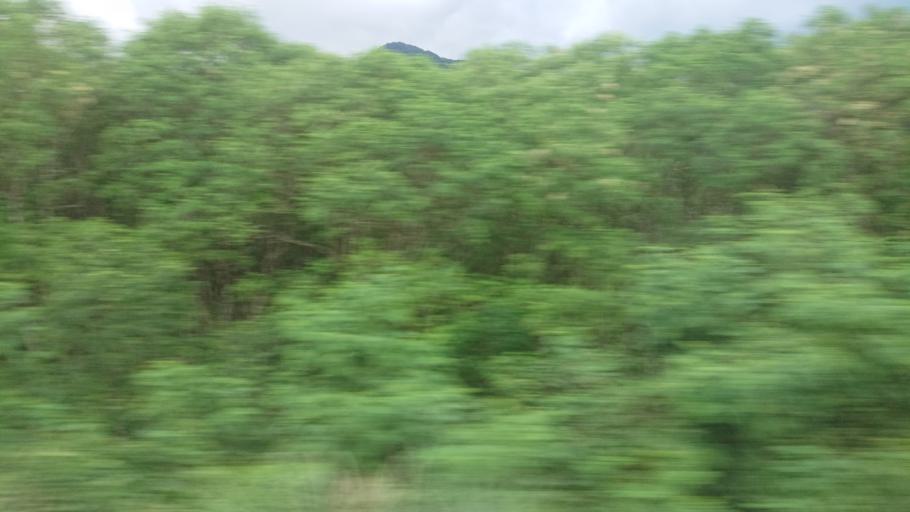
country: TW
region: Taiwan
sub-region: Hualien
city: Hualian
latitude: 23.6191
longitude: 121.3951
